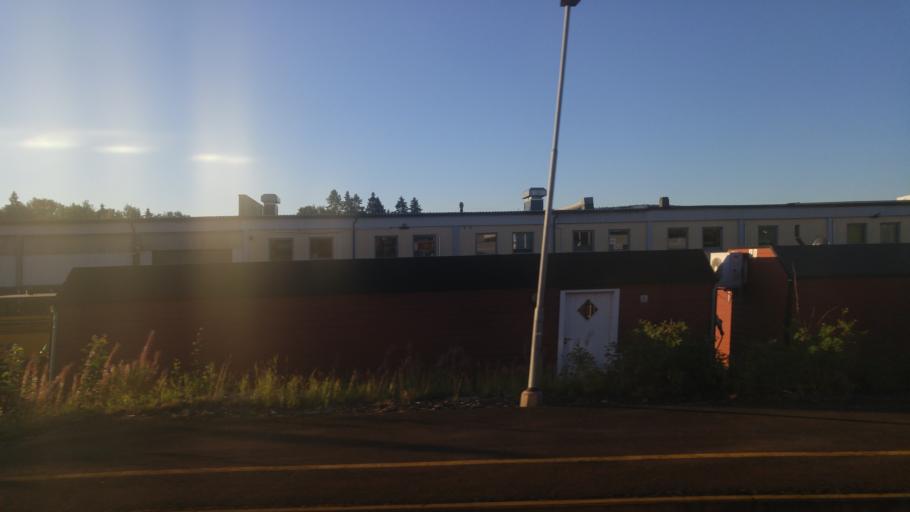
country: NO
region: Akershus
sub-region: Lorenskog
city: Kjenn
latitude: 59.9446
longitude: 10.8735
